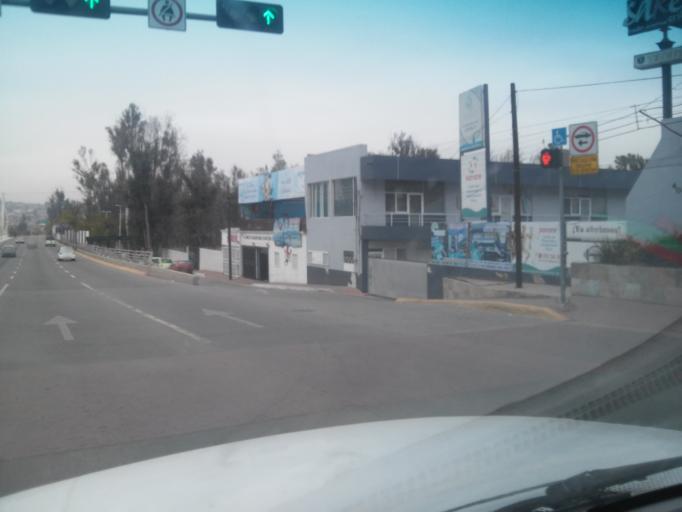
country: MX
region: Durango
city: Victoria de Durango
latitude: 24.0221
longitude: -104.6900
